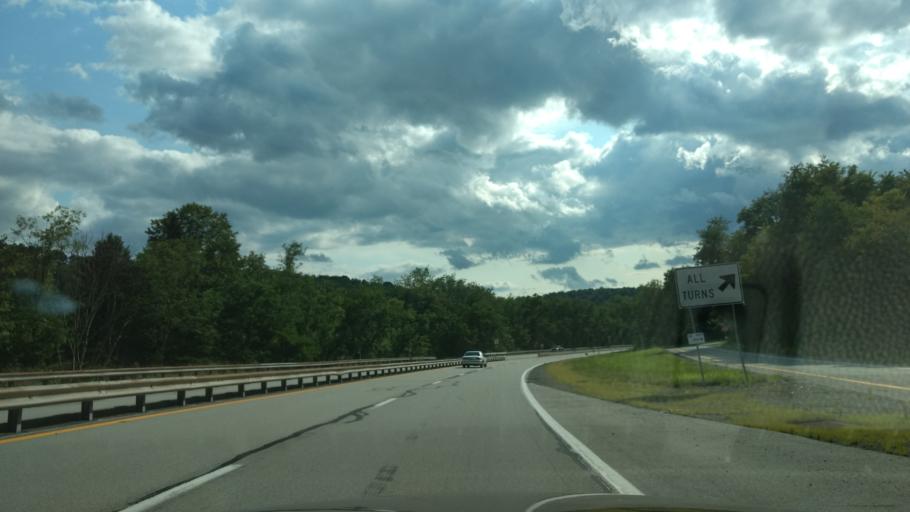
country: US
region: Pennsylvania
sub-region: Westmoreland County
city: Murrysville
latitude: 40.5125
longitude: -79.6463
